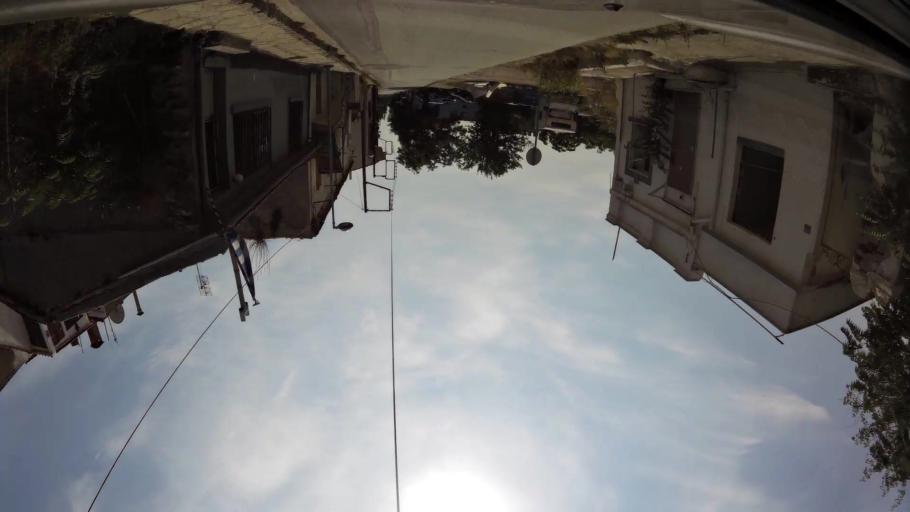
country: GR
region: Central Macedonia
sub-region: Nomos Thessalonikis
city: Sykies
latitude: 40.6438
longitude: 22.9533
